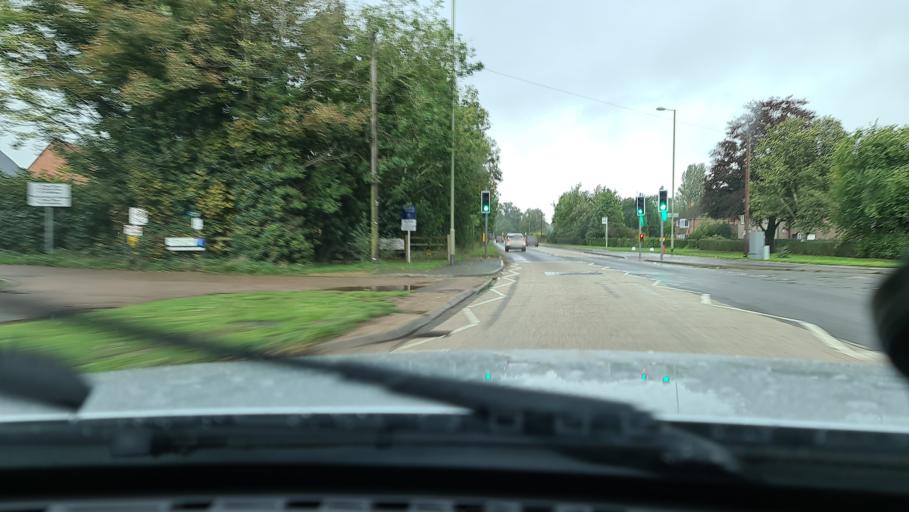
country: GB
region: England
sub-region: Oxfordshire
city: Adderbury
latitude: 52.0398
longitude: -1.3243
